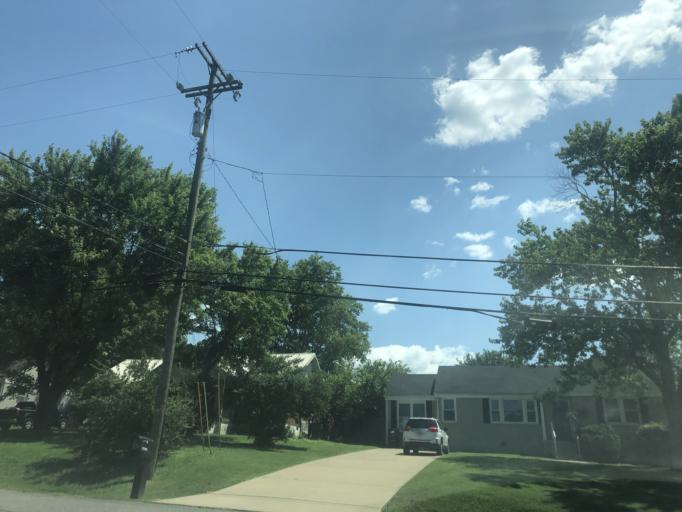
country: US
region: Tennessee
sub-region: Davidson County
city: Nashville
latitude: 36.1882
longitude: -86.7149
